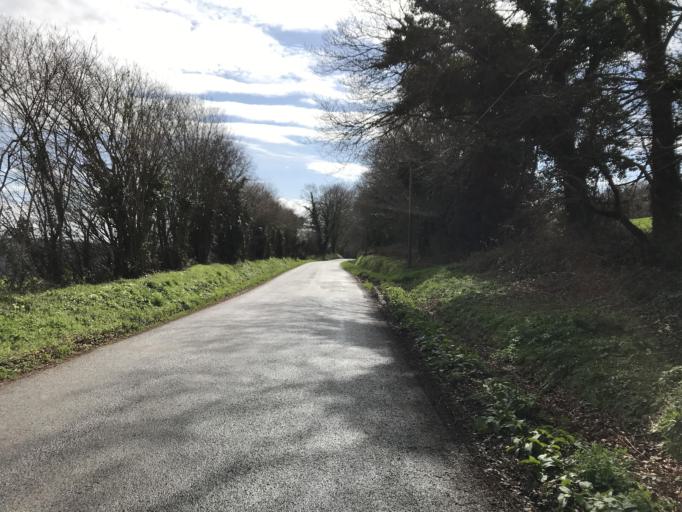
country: FR
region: Brittany
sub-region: Departement du Finistere
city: Daoulas
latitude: 48.3731
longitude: -4.2711
